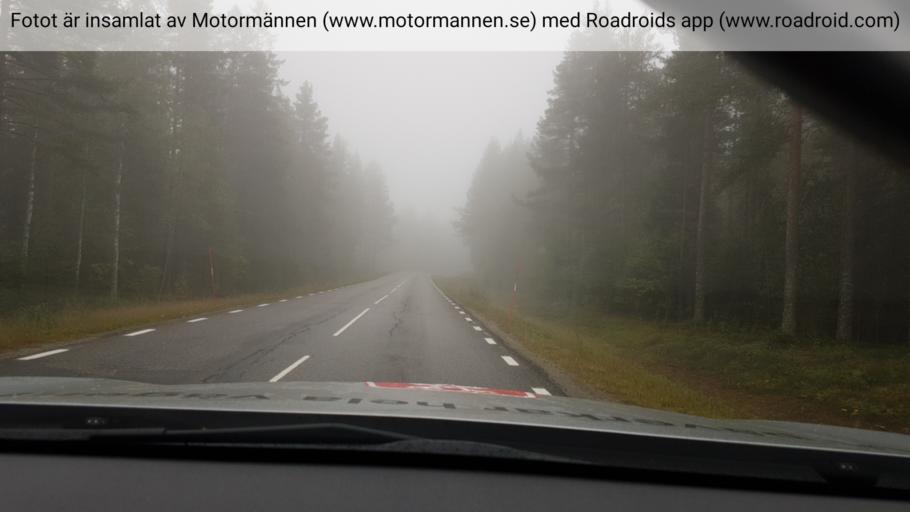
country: SE
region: Vaesterbotten
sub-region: Umea Kommun
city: Ersmark
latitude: 64.1380
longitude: 20.1638
